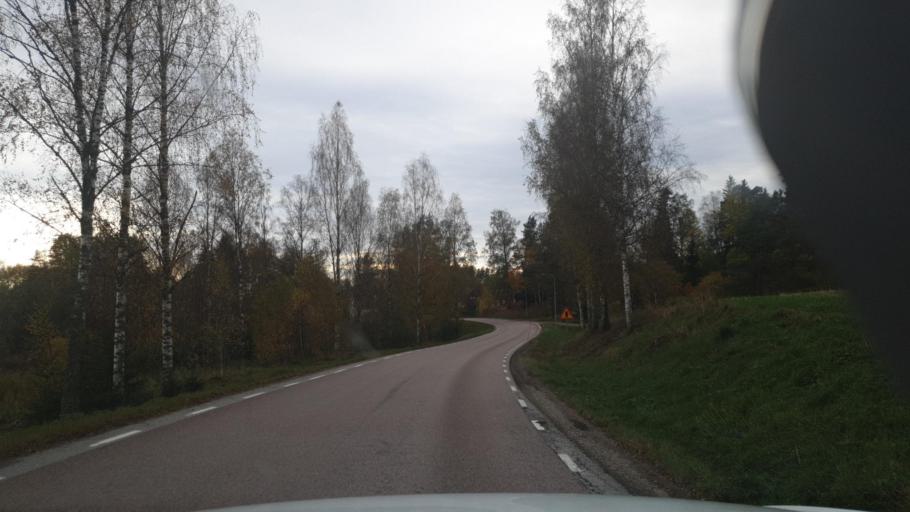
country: SE
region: Vaermland
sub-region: Arvika Kommun
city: Arvika
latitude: 59.6892
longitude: 12.7893
